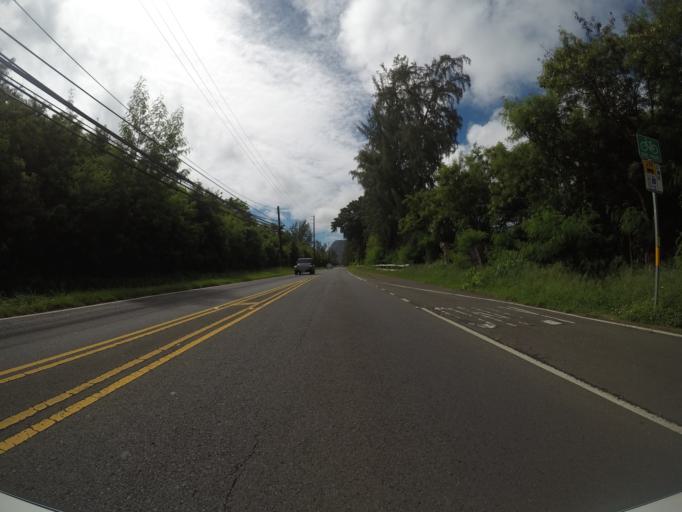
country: US
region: Hawaii
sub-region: Honolulu County
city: Waimanalo
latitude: 21.3449
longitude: -157.7098
